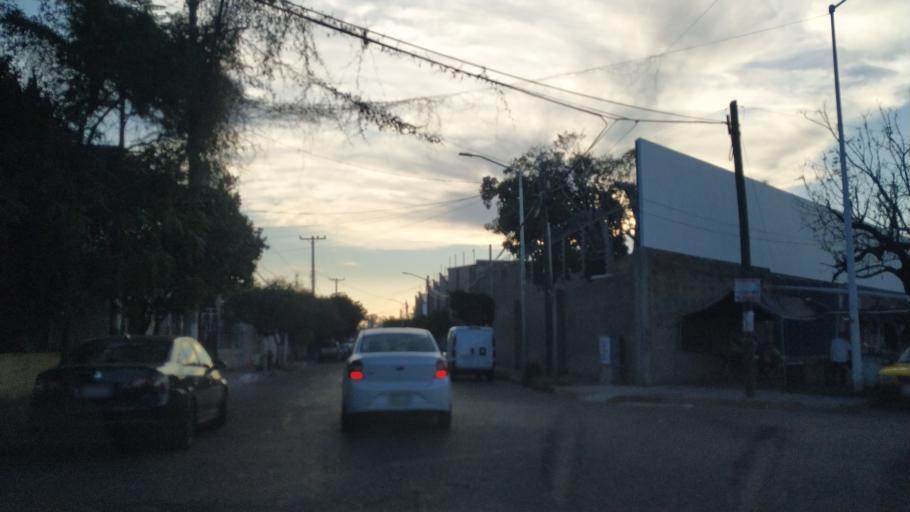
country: MX
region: Jalisco
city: Tlaquepaque
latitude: 20.6512
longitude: -103.3264
